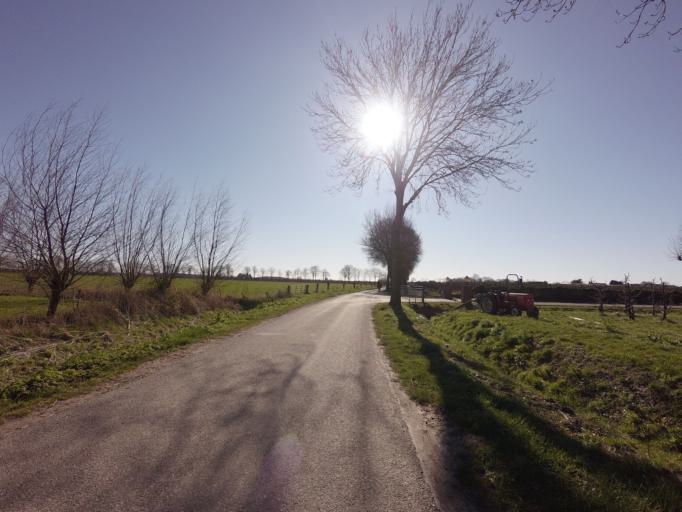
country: NL
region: Gelderland
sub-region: Gemeente Buren
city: Lienden
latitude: 51.9642
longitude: 5.5040
